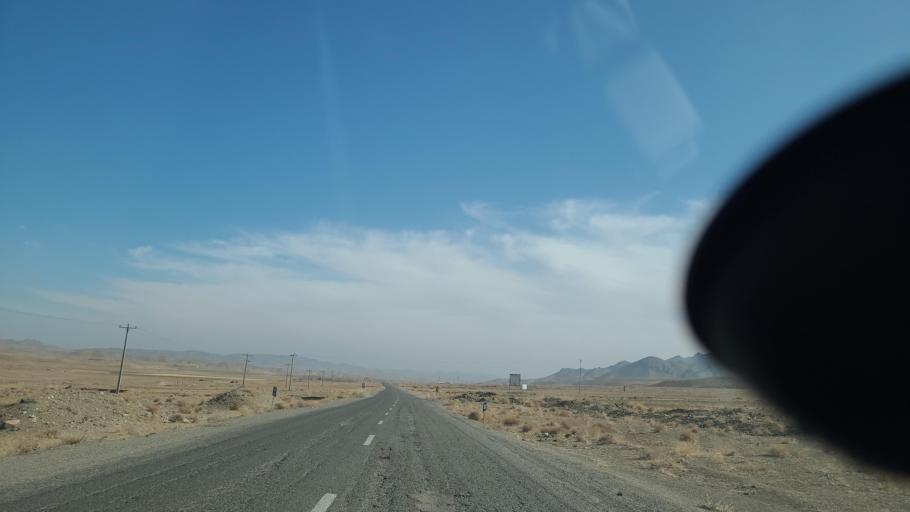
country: IR
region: Razavi Khorasan
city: Fariman
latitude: 35.5872
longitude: 59.6482
